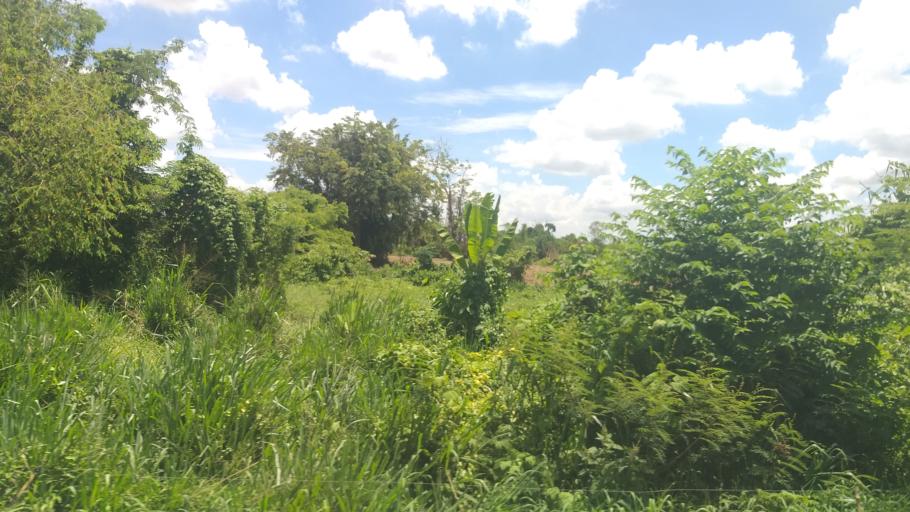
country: TH
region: Nakhon Nayok
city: Ban Na
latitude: 14.2787
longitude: 101.0664
